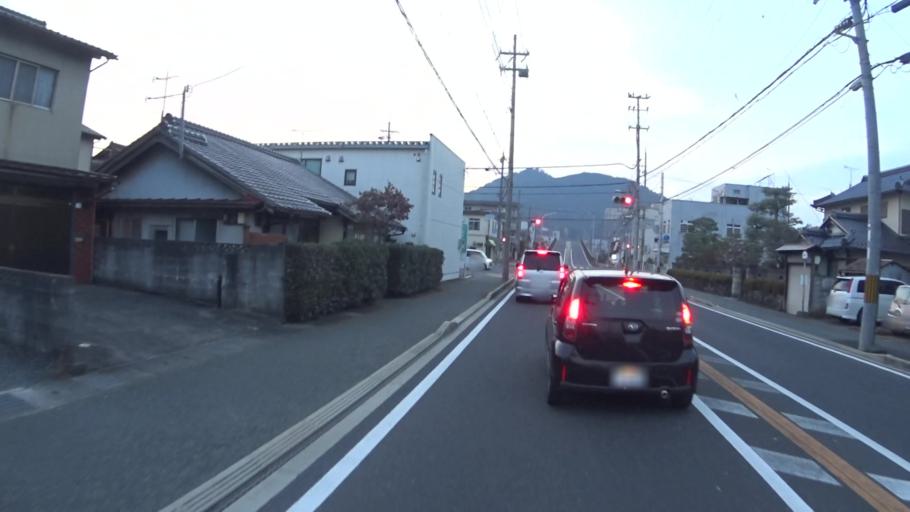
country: JP
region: Kyoto
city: Maizuru
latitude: 35.4450
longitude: 135.3339
